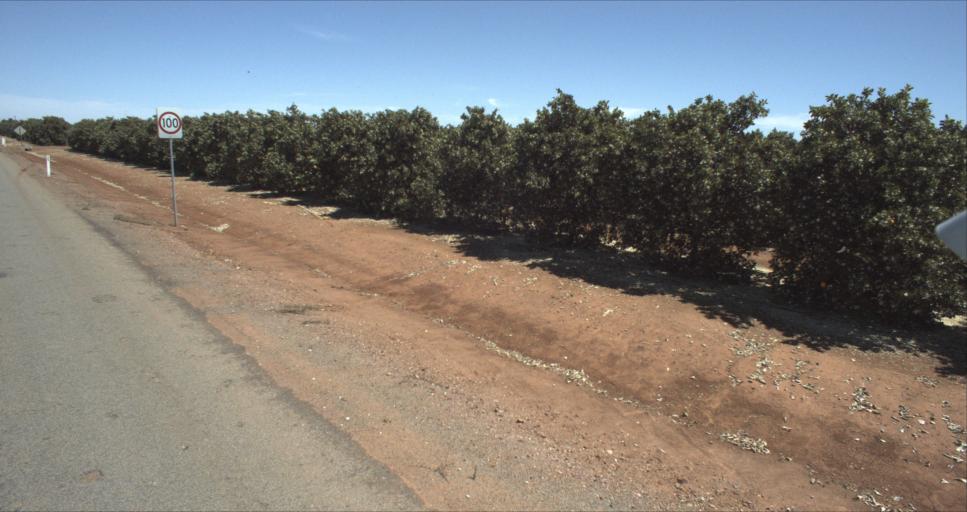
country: AU
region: New South Wales
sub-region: Leeton
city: Leeton
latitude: -34.5314
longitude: 146.3289
